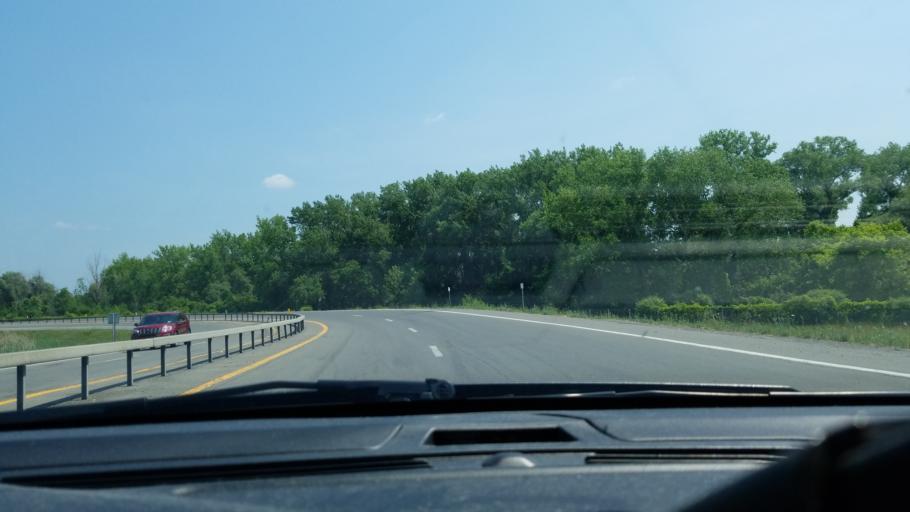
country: US
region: New York
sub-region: Onondaga County
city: Galeville
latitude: 43.0888
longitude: -76.1649
